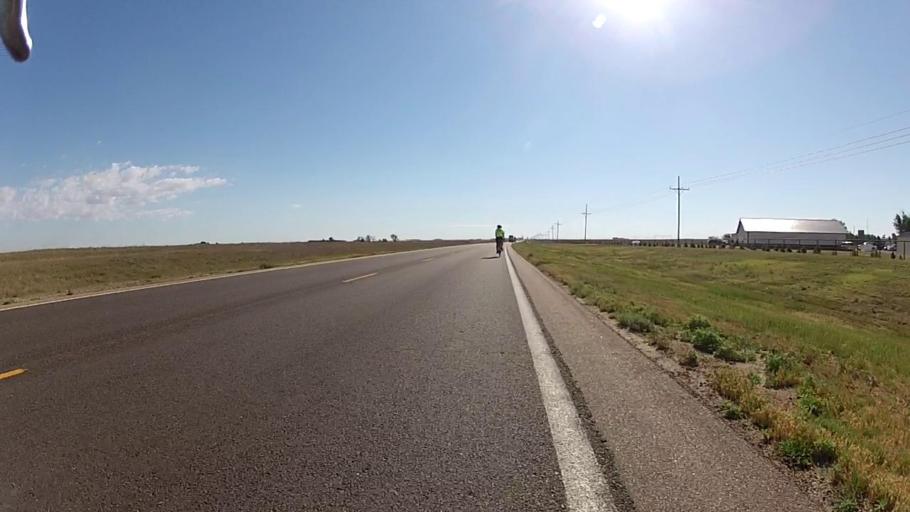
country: US
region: Kansas
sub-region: Gray County
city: Cimarron
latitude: 37.5777
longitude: -100.5195
